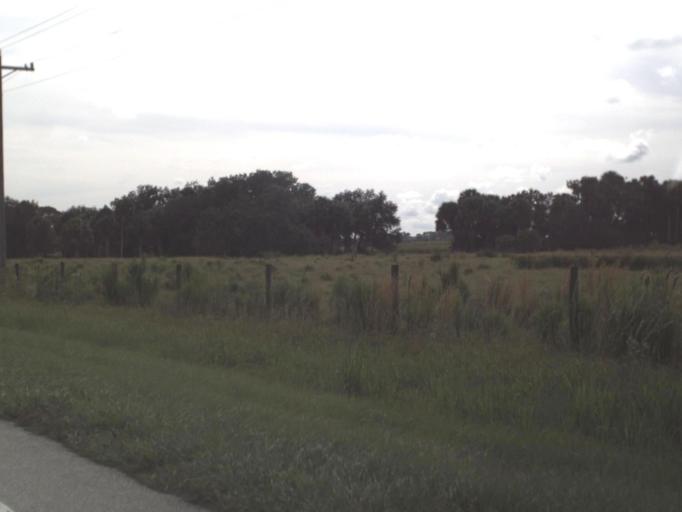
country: US
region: Florida
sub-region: Highlands County
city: Placid Lakes
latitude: 27.2089
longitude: -81.4289
